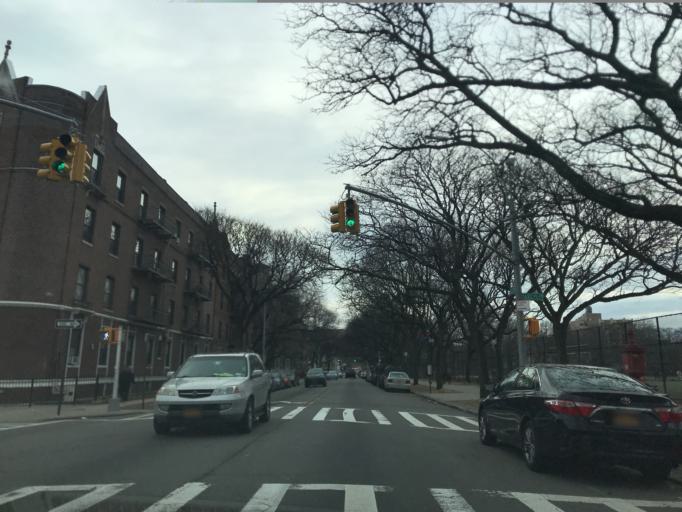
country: US
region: New York
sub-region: Kings County
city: Brooklyn
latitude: 40.6498
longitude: -73.9676
